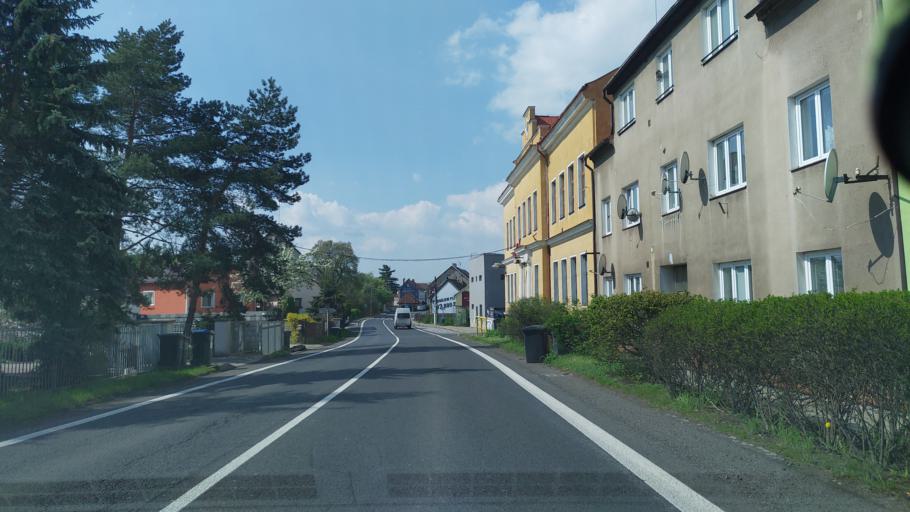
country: CZ
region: Ustecky
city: Krupka
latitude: 50.6743
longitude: 13.8969
